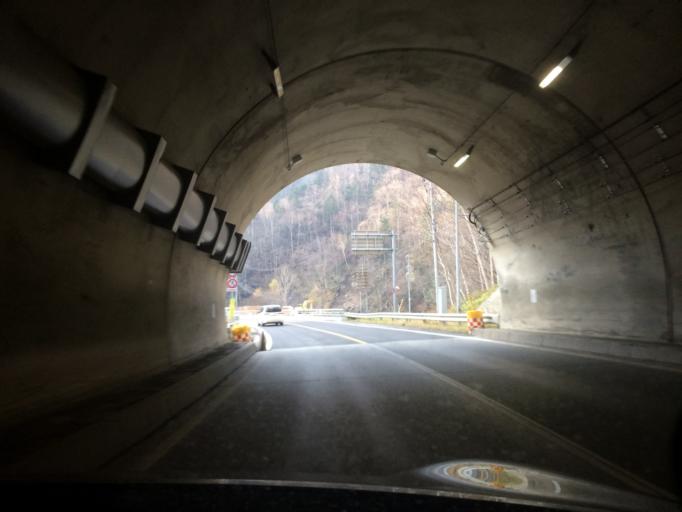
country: JP
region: Hokkaido
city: Shimo-furano
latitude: 42.9472
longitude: 142.5983
